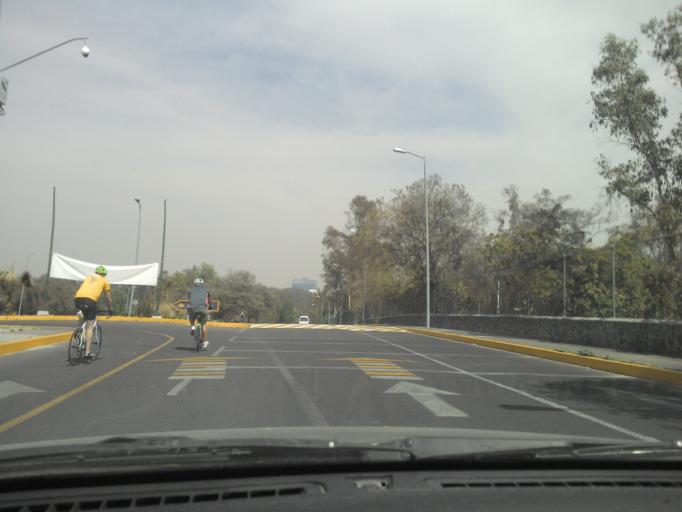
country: MX
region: Mexico City
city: Magdalena Contreras
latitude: 19.3217
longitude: -99.1892
